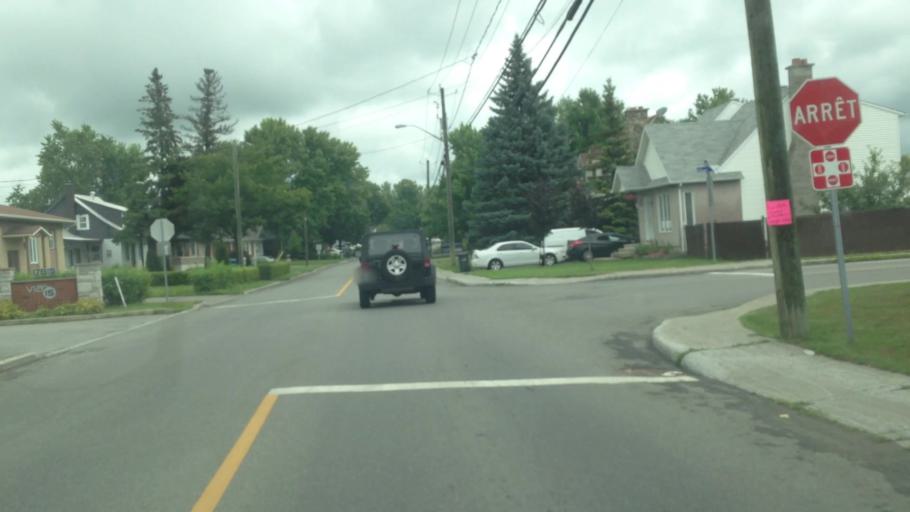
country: CA
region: Quebec
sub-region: Laurentides
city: Blainville
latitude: 45.6998
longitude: -73.9294
